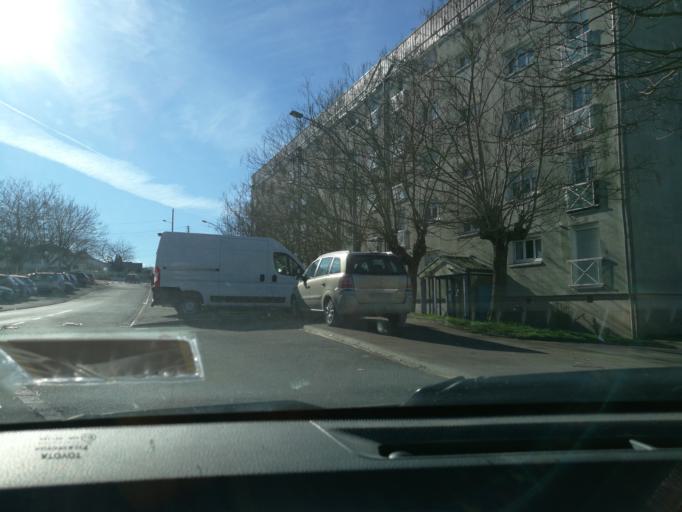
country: FR
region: Centre
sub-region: Departement du Loiret
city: Saint-Jean-de-la-Ruelle
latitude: 47.9040
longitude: 1.8761
